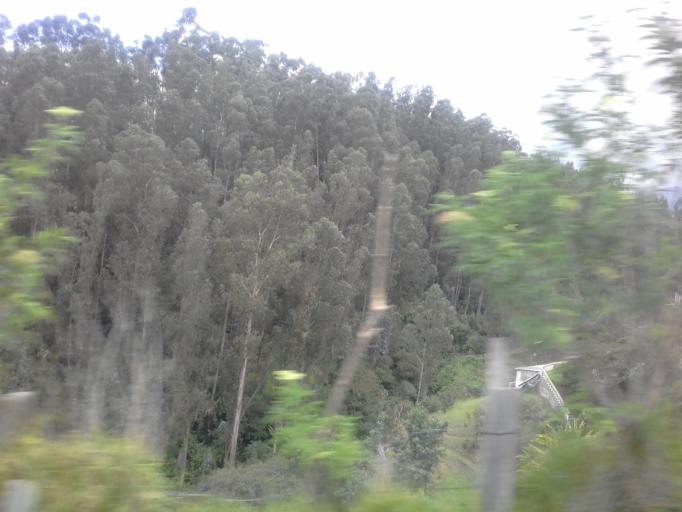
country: EC
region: Pichincha
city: Sangolqui
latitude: -0.3314
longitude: -78.4165
